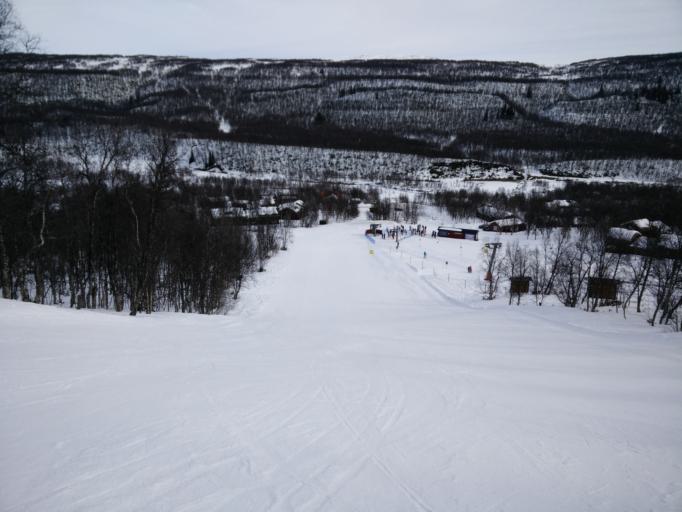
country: NO
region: Sor-Trondelag
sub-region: Tydal
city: Aas
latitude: 62.7049
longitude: 12.3763
